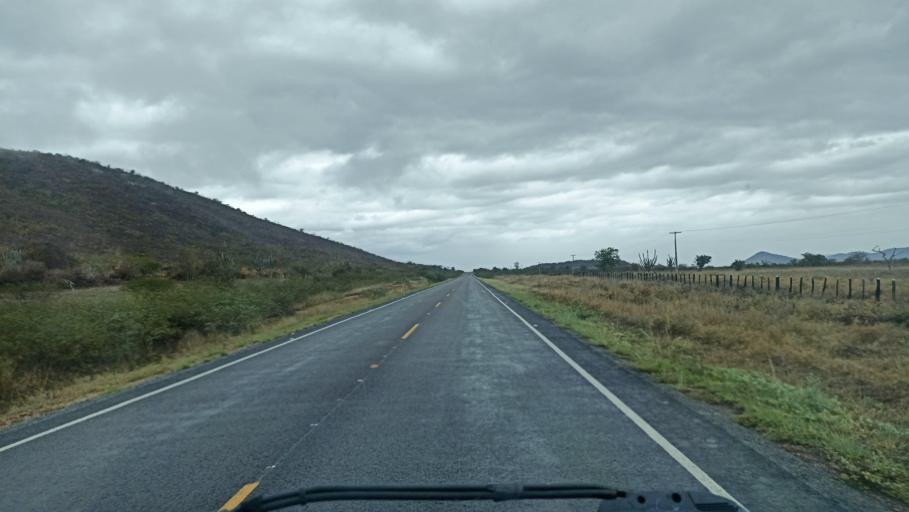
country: BR
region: Bahia
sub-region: Iacu
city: Iacu
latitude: -12.9562
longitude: -40.4679
